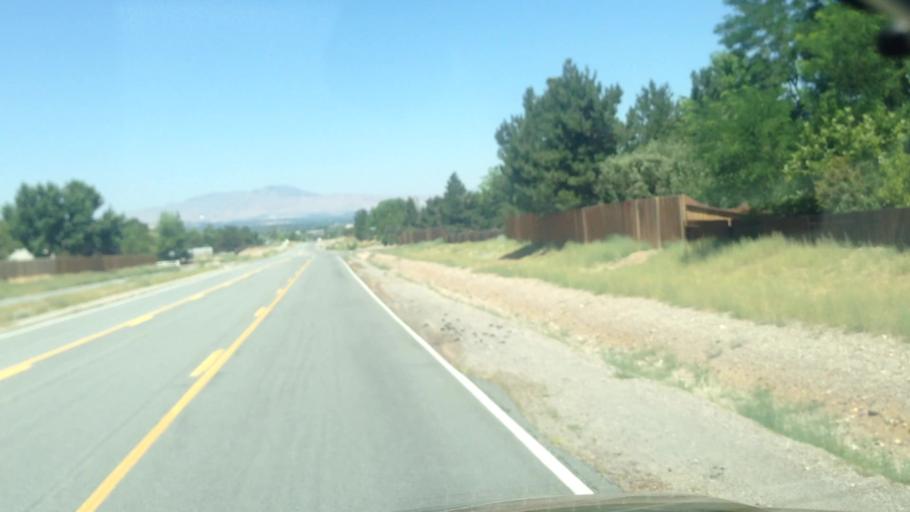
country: US
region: Nevada
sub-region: Storey County
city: Virginia City
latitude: 39.3867
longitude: -119.7265
